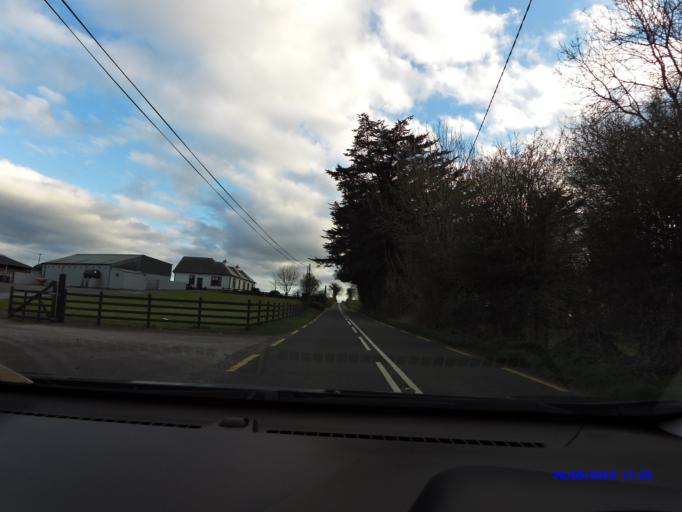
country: IE
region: Connaught
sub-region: Maigh Eo
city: Ballyhaunis
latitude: 53.7490
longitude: -8.7511
